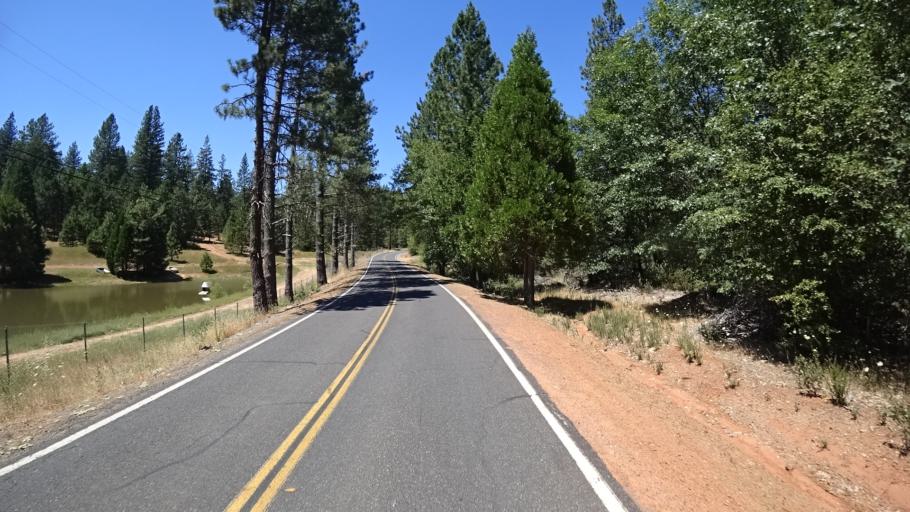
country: US
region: California
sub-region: Calaveras County
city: Mountain Ranch
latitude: 38.3117
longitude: -120.5195
